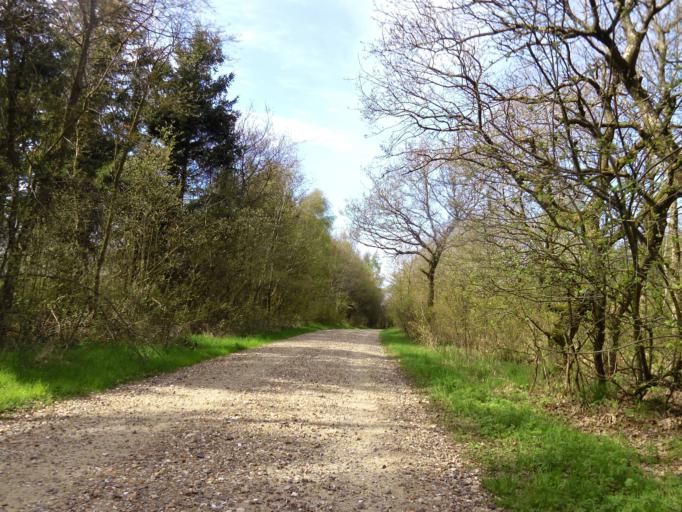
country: DK
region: Central Jutland
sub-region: Holstebro Kommune
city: Vinderup
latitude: 56.4785
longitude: 8.8723
